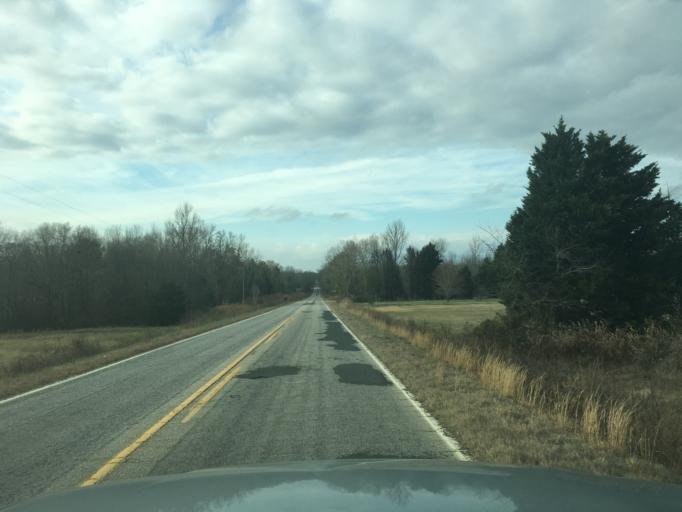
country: US
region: South Carolina
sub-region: Abbeville County
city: Due West
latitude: 34.3462
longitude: -82.4966
